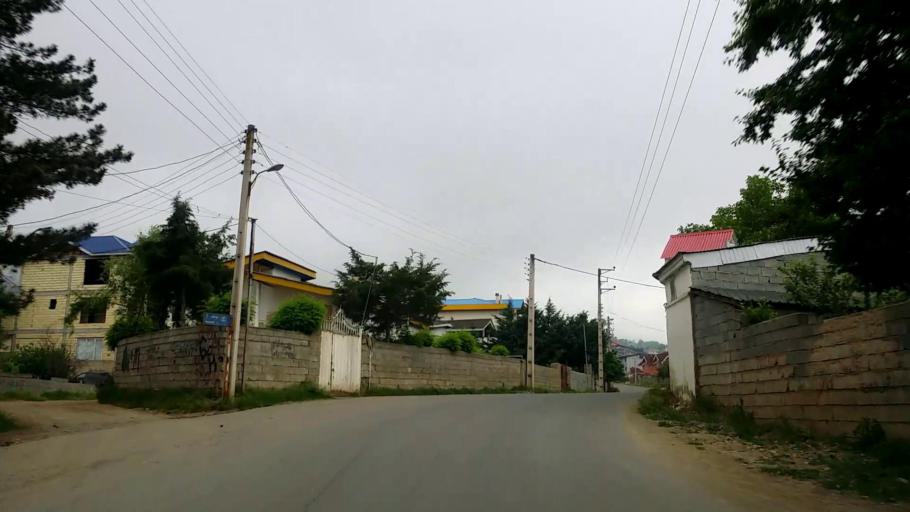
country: IR
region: Mazandaran
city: `Abbasabad
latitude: 36.5022
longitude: 51.1596
